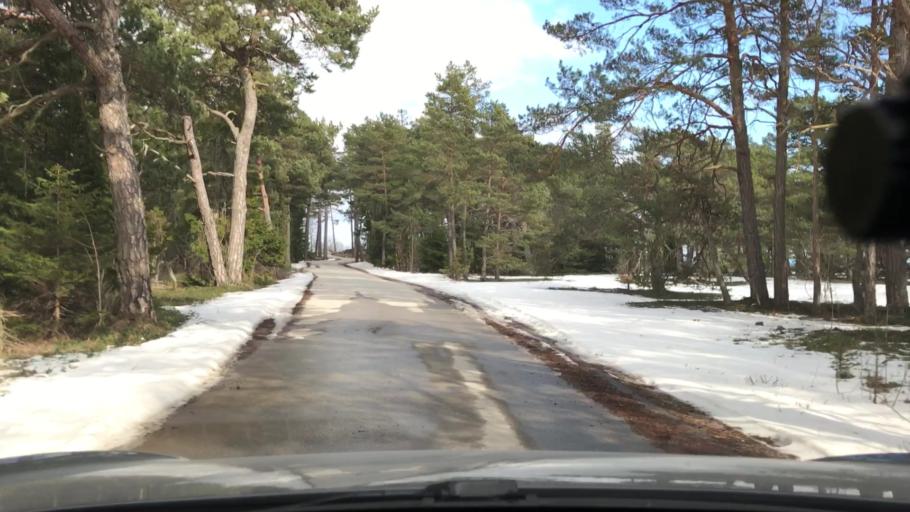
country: SE
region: Gotland
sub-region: Gotland
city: Hemse
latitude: 57.3435
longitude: 18.7267
